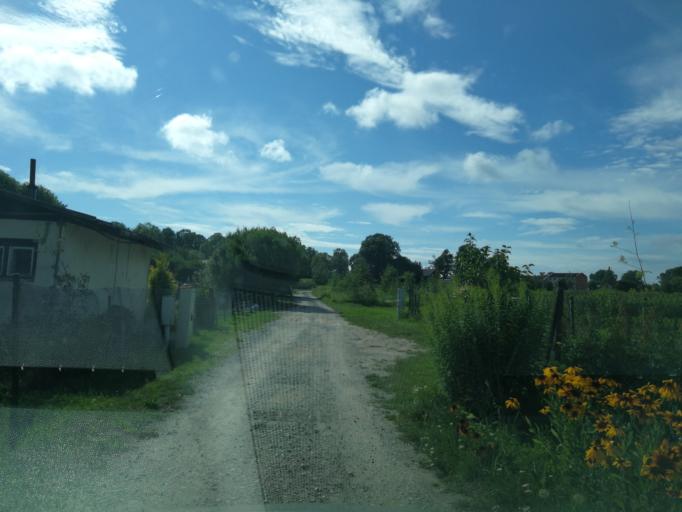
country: LV
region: Adazi
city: Adazi
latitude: 57.0944
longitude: 24.3207
